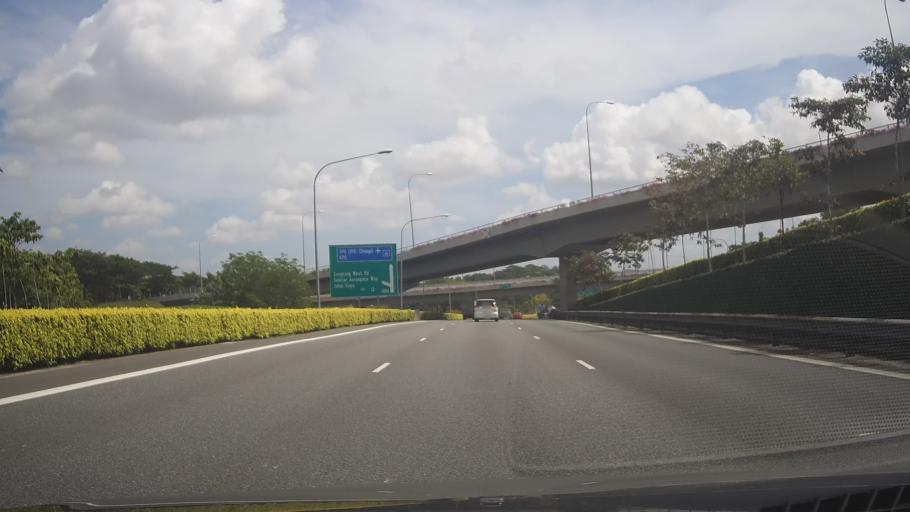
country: MY
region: Johor
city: Kampung Pasir Gudang Baru
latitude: 1.3990
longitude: 103.8552
